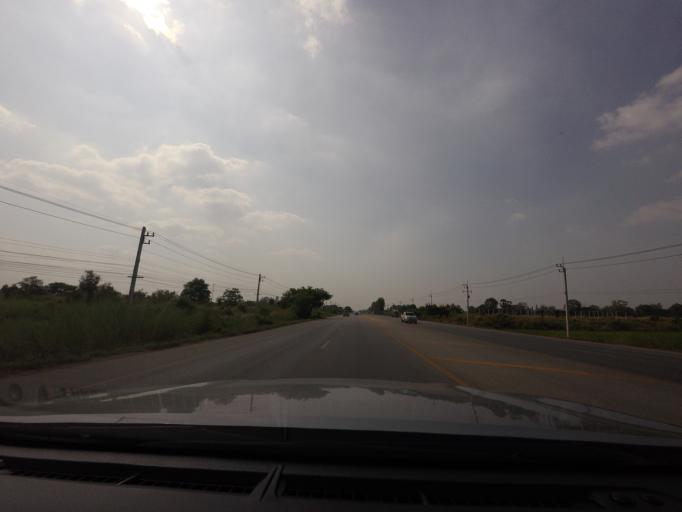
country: TH
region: Phitsanulok
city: Bang Rakam
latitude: 16.7689
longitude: 100.1512
